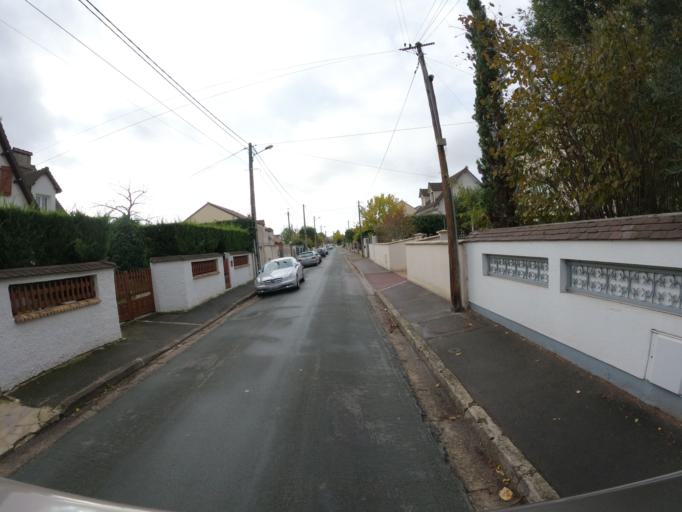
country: FR
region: Ile-de-France
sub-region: Departement de Seine-Saint-Denis
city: Coubron
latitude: 48.9111
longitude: 2.5917
